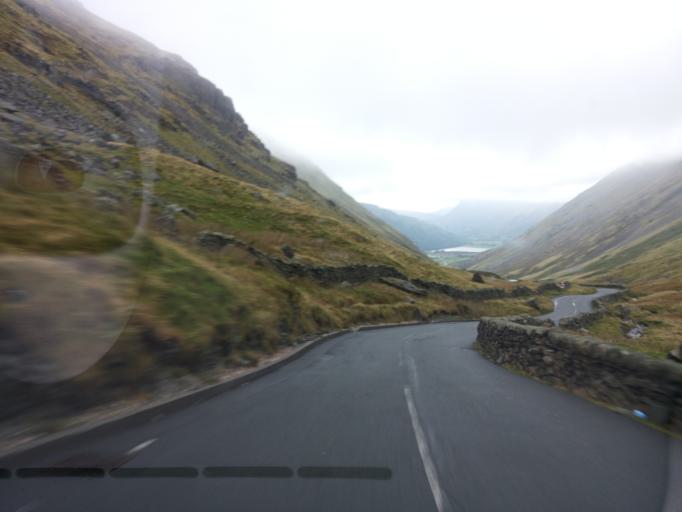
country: GB
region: England
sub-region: Cumbria
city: Ambleside
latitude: 54.4704
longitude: -2.9232
